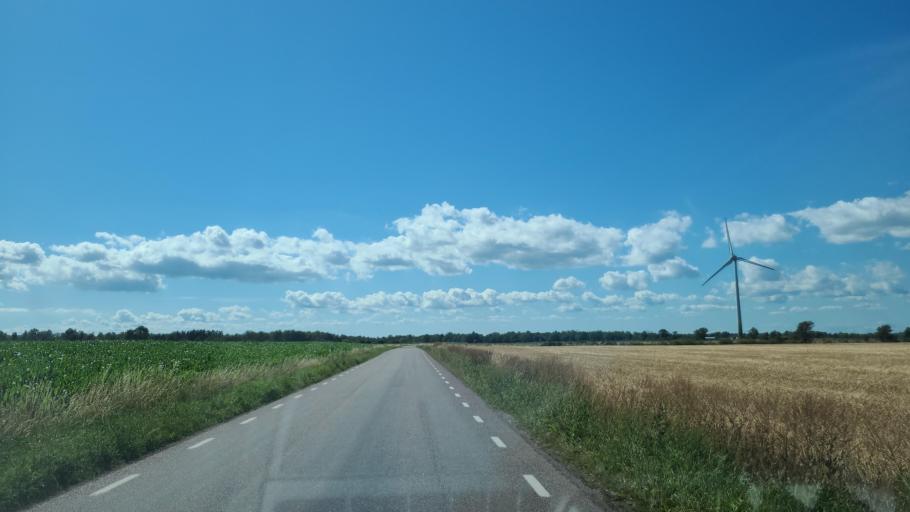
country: SE
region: Kalmar
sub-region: Borgholms Kommun
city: Borgholm
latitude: 56.7810
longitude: 16.7265
